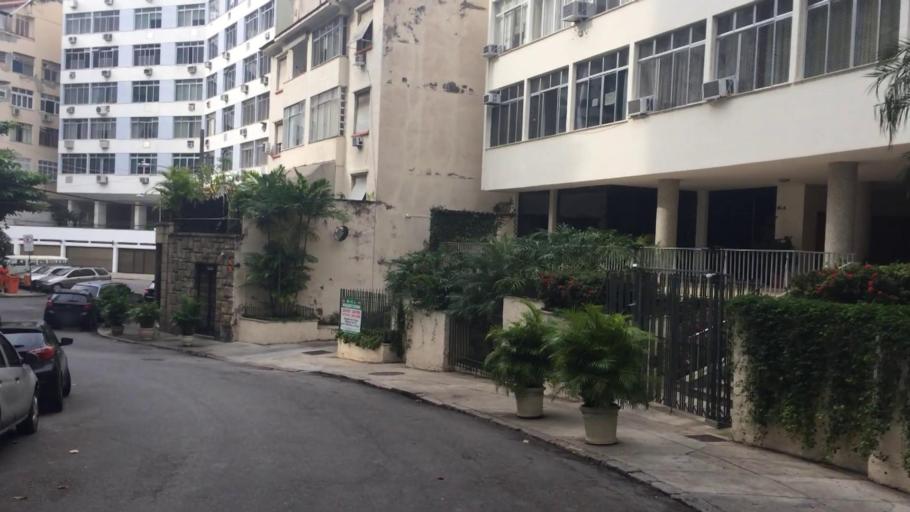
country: BR
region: Rio de Janeiro
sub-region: Rio De Janeiro
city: Rio de Janeiro
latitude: -22.9430
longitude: -43.1921
